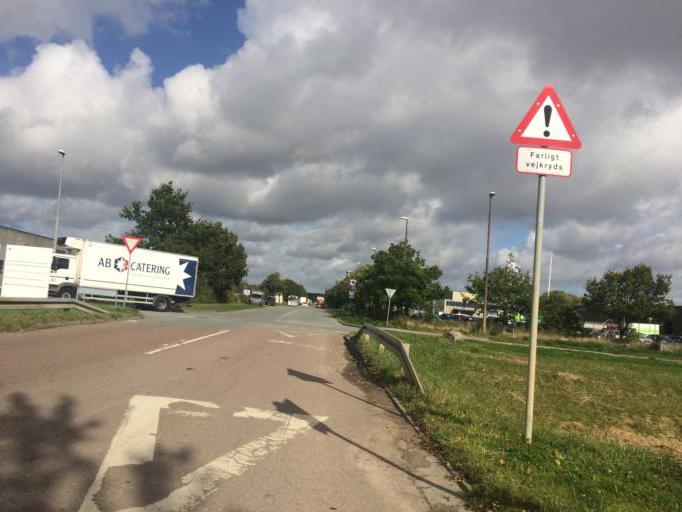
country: DK
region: Capital Region
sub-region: Hvidovre Kommune
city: Hvidovre
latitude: 55.6057
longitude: 12.4678
